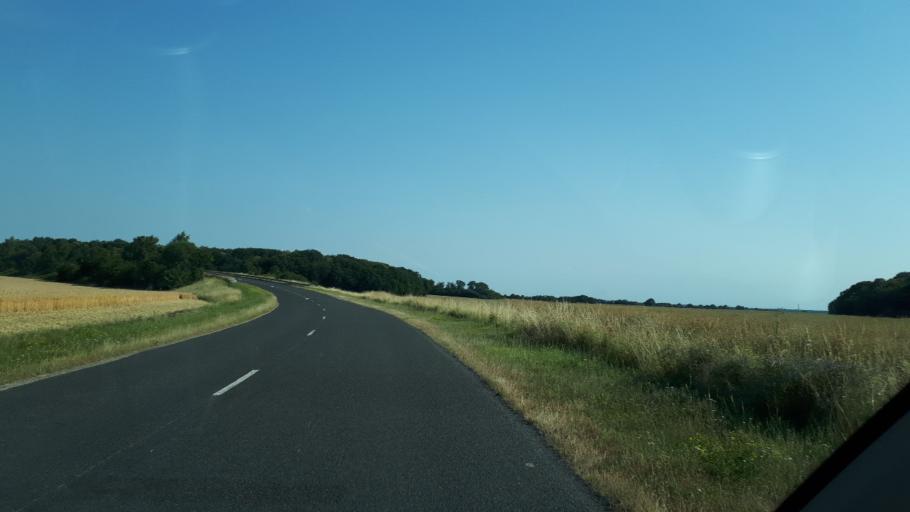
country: FR
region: Centre
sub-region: Departement du Loir-et-Cher
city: La Ville-aux-Clercs
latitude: 47.9722
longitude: 1.0471
